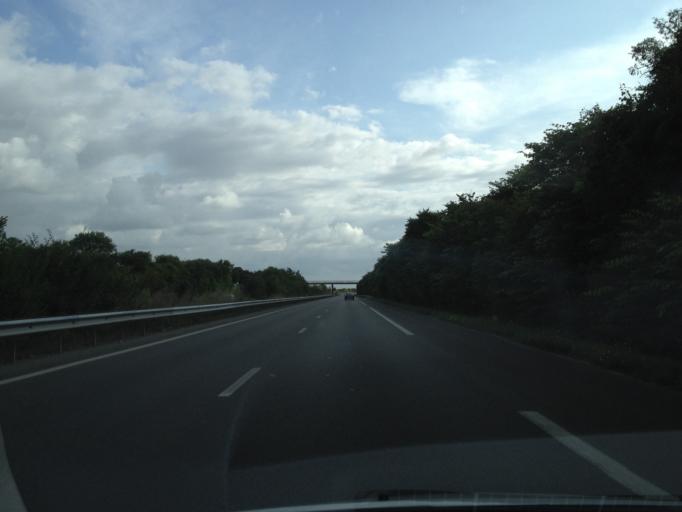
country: FR
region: Poitou-Charentes
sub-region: Departement de la Charente-Maritime
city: Dompierre-sur-Mer
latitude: 46.1876
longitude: -1.0743
